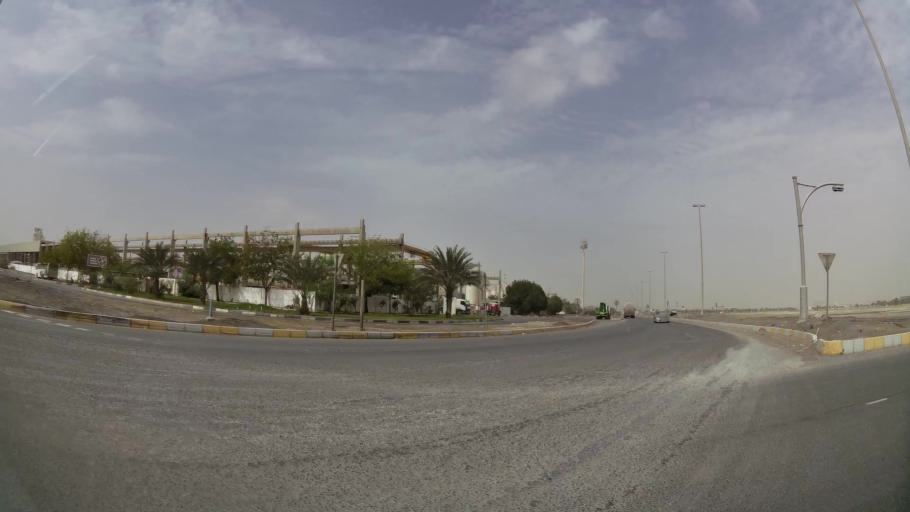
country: AE
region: Abu Dhabi
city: Abu Dhabi
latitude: 24.3375
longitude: 54.5126
